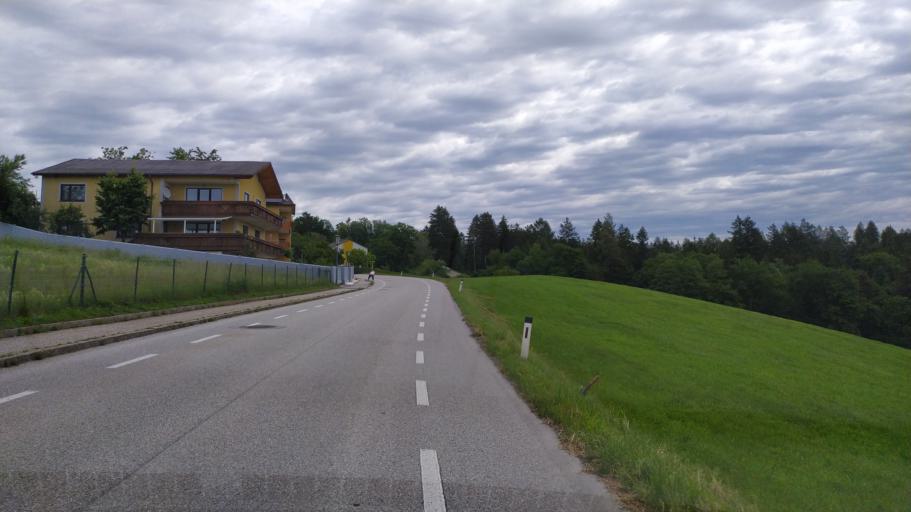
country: AT
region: Upper Austria
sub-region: Politischer Bezirk Perg
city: Perg
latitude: 48.2579
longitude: 14.6470
